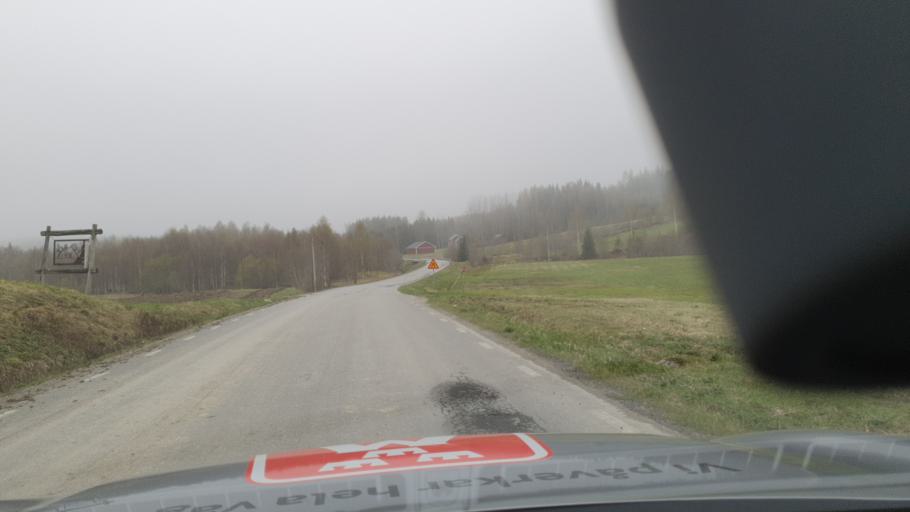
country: SE
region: Vaesternorrland
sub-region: OErnskoeldsviks Kommun
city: Husum
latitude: 63.5761
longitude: 19.0235
